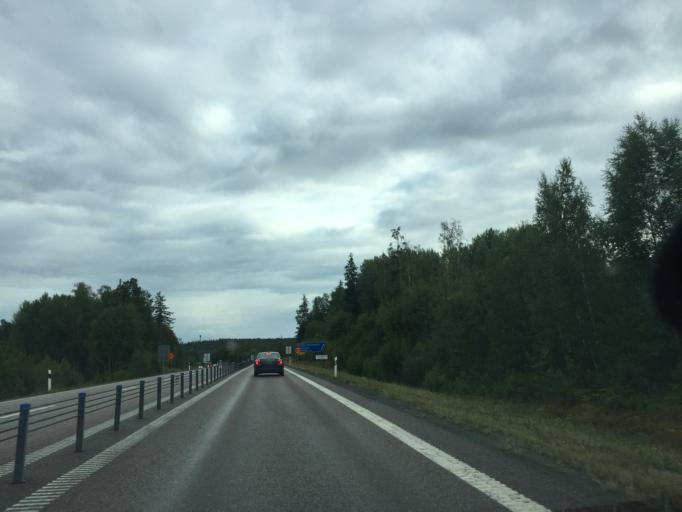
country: SE
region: Vaestmanland
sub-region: Arboga Kommun
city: Arboga
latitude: 59.4088
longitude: 15.8855
